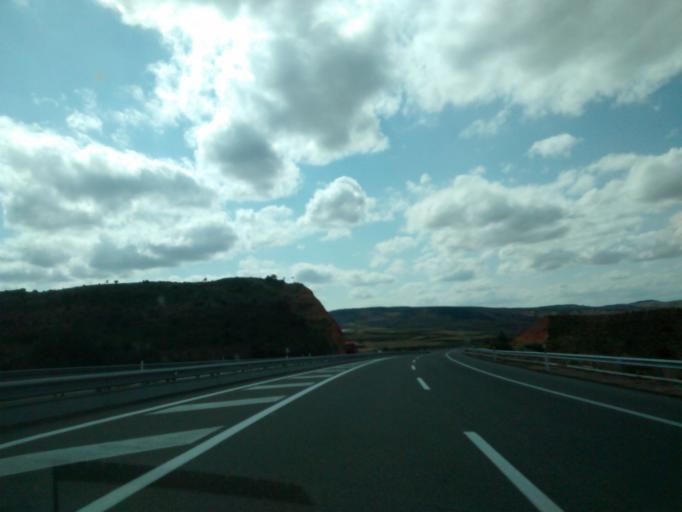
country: ES
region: Castille and Leon
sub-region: Provincia de Soria
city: Arcos de Jalon
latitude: 41.2020
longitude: -2.3290
